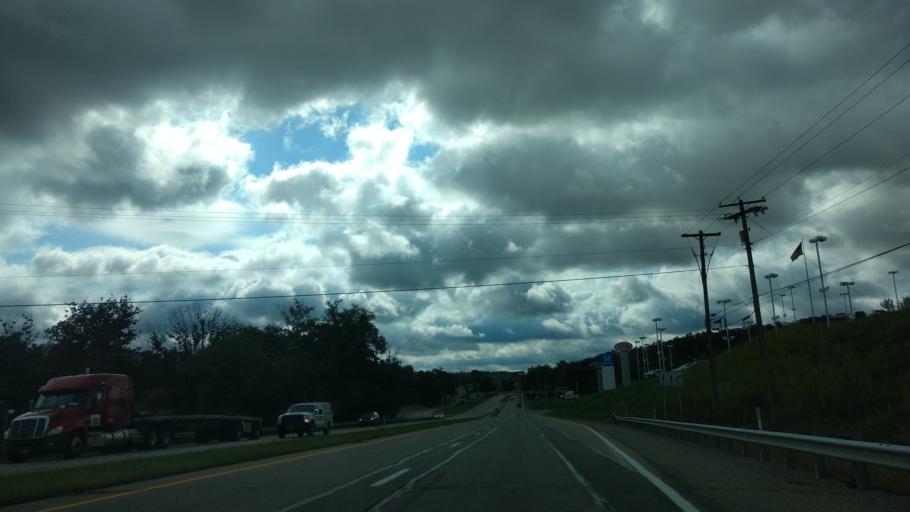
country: US
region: Pennsylvania
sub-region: Westmoreland County
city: Fellsburg
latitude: 40.1647
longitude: -79.7855
